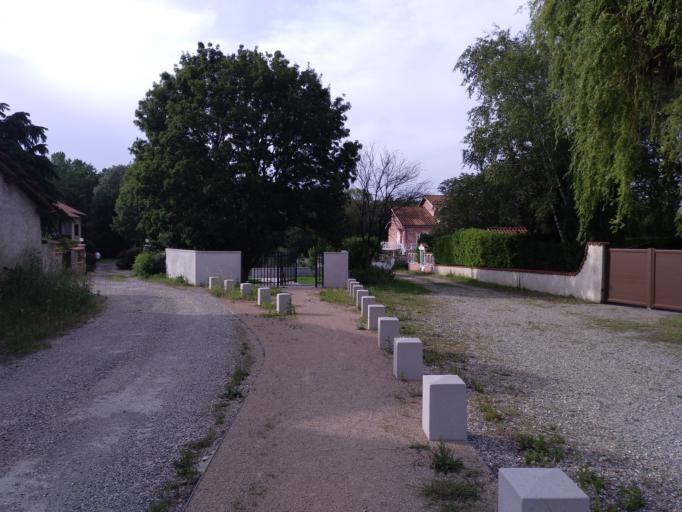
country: FR
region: Rhone-Alpes
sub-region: Departement du Rhone
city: Marennes
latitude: 45.6307
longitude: 4.9264
